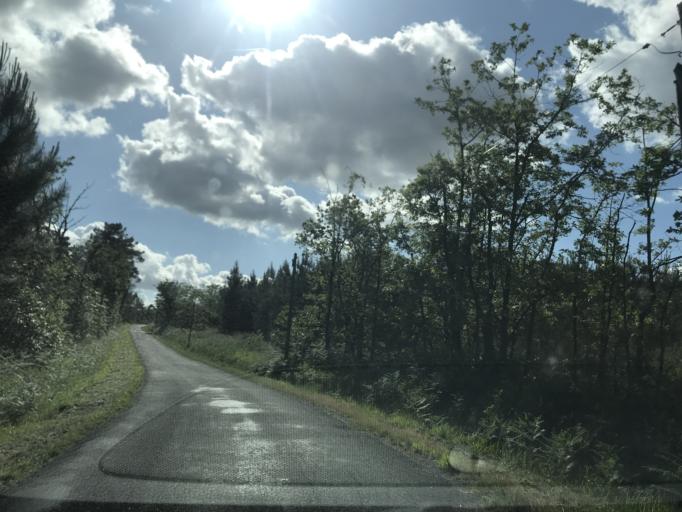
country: FR
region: Poitou-Charentes
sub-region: Departement de la Charente
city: Chalais
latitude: 45.2787
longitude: -0.0390
